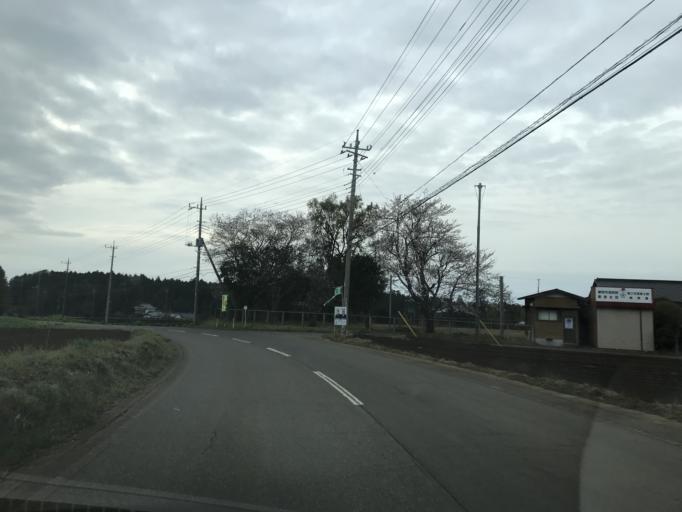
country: JP
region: Chiba
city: Omigawa
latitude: 35.8078
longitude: 140.5472
